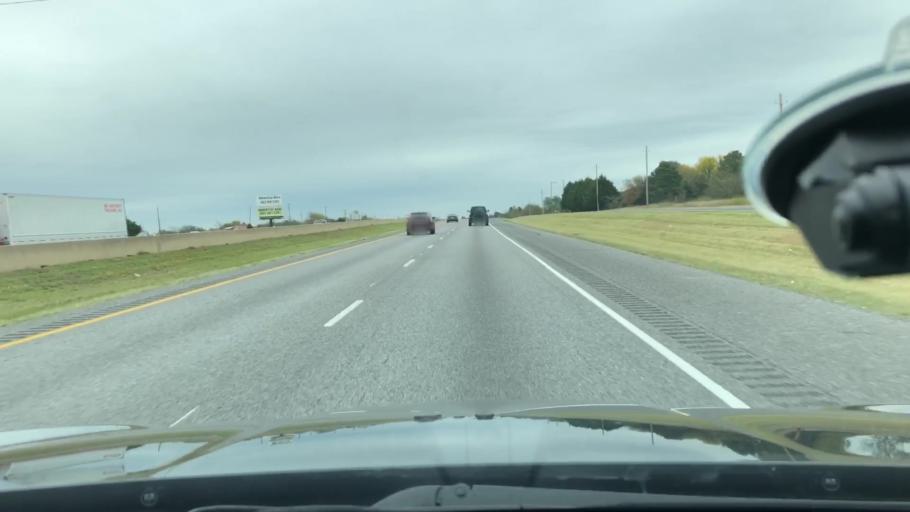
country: US
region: Texas
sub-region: Hunt County
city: Greenville
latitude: 33.1332
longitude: -96.0377
